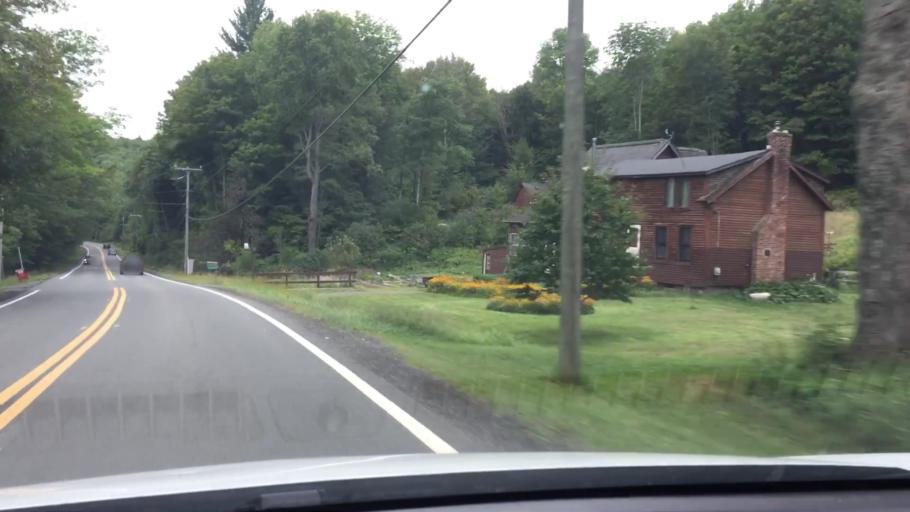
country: US
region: Massachusetts
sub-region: Berkshire County
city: Hinsdale
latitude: 42.3840
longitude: -73.1225
